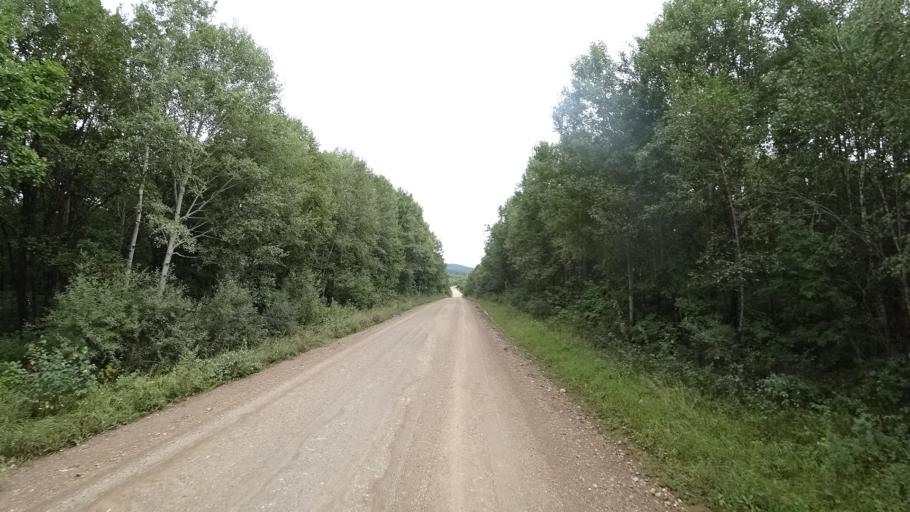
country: RU
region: Primorskiy
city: Lyalichi
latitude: 44.0852
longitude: 132.4420
